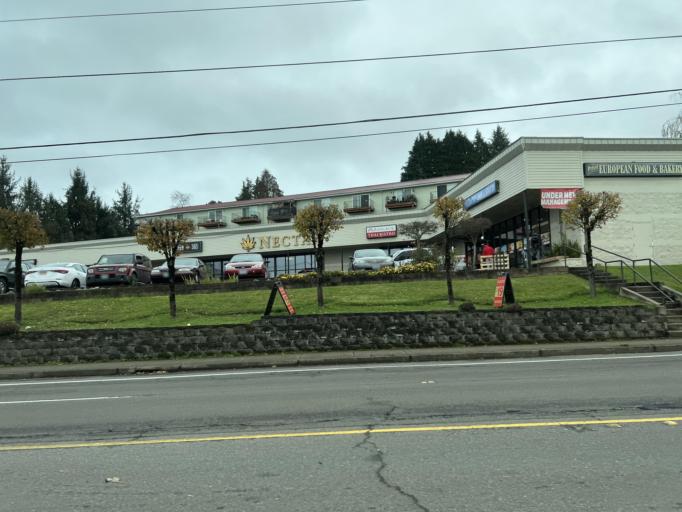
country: US
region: Oregon
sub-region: Marion County
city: Salem
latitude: 44.8855
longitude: -123.0324
